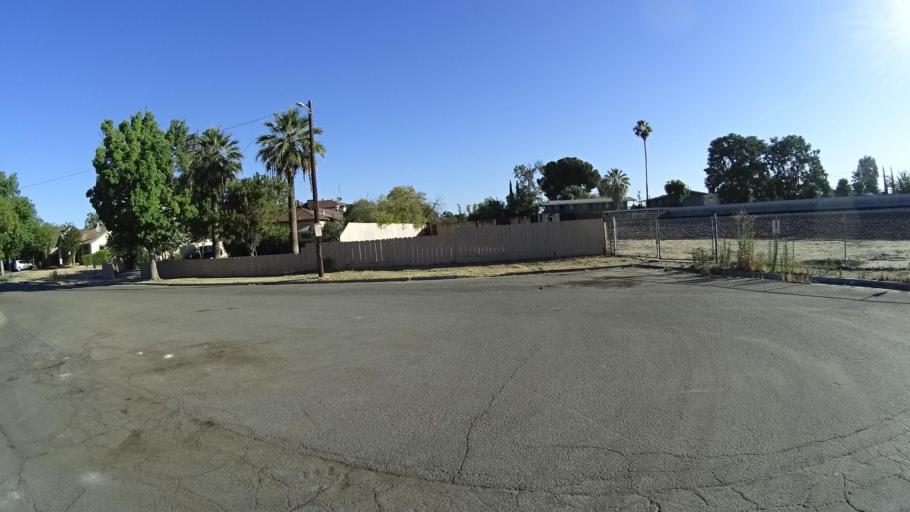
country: US
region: California
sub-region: Fresno County
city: Fresno
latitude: 36.7703
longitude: -119.7958
